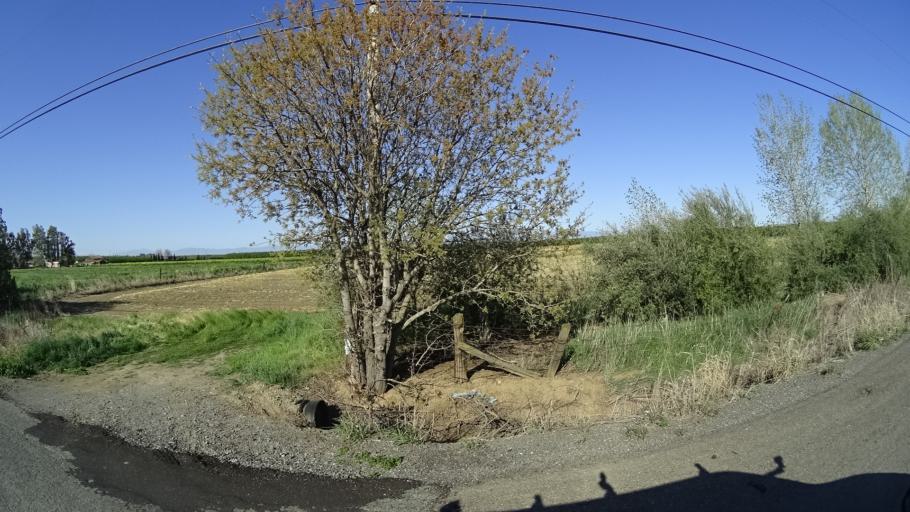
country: US
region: California
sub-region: Glenn County
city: Orland
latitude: 39.8062
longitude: -122.1041
